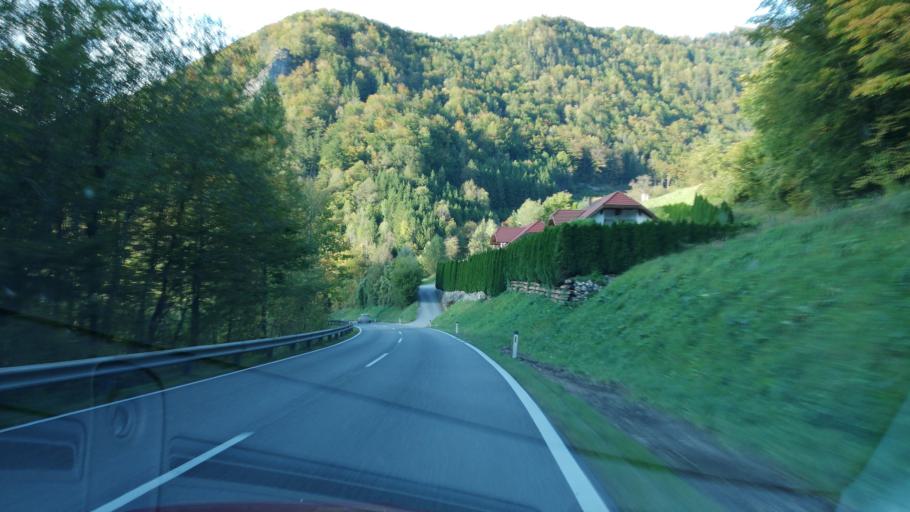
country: AT
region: Upper Austria
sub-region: Politischer Bezirk Steyr-Land
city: Maria Neustift
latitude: 47.8765
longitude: 14.6033
